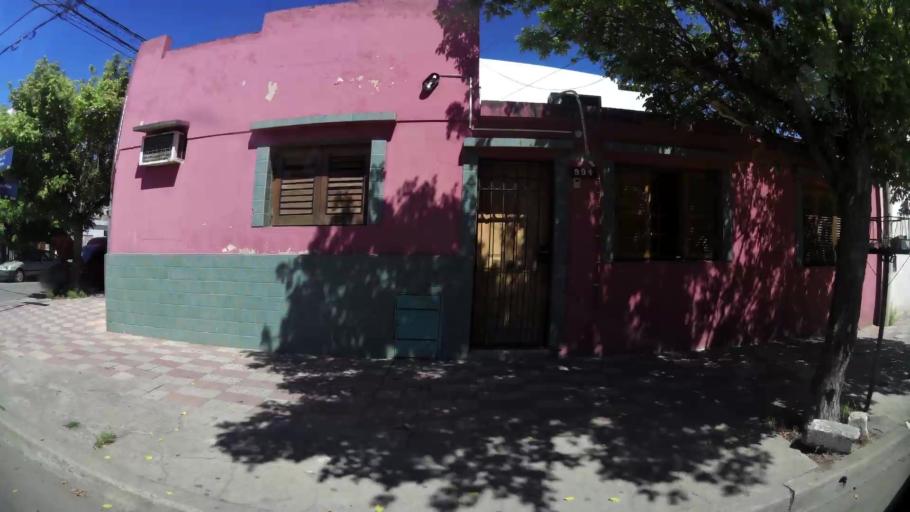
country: AR
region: Cordoba
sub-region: Departamento de Capital
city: Cordoba
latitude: -31.4206
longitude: -64.1414
